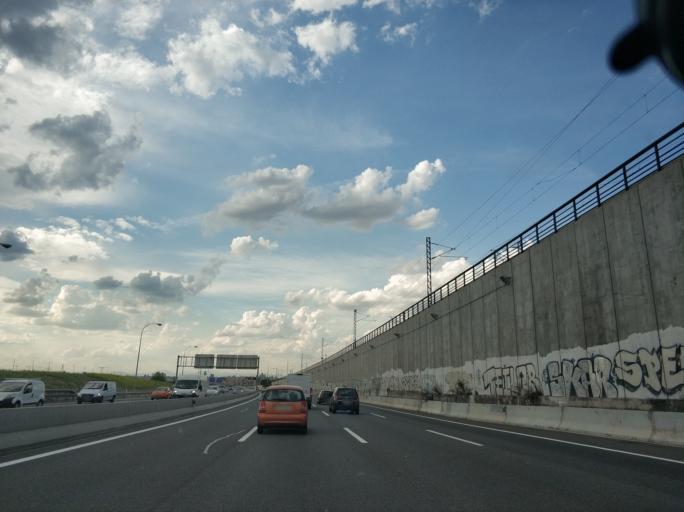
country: ES
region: Madrid
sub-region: Provincia de Madrid
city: Usera
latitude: 40.3696
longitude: -3.6788
